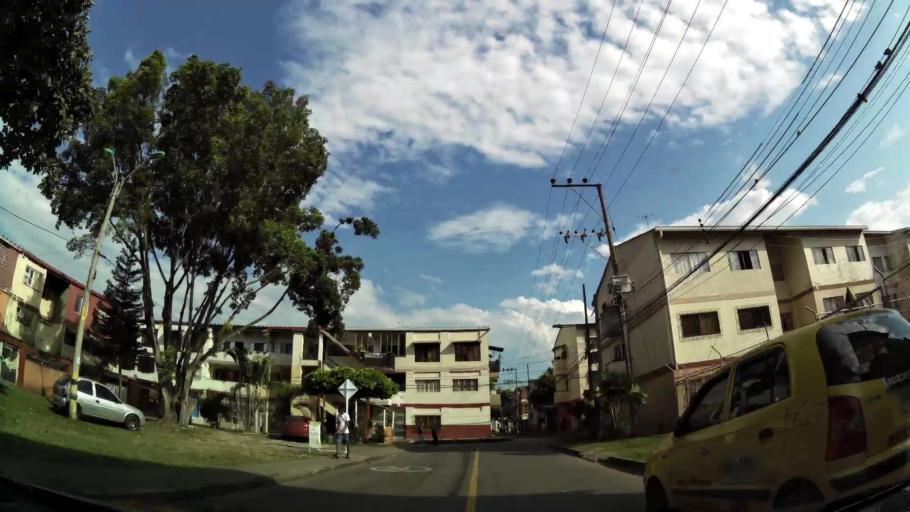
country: CO
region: Valle del Cauca
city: Cali
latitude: 3.4679
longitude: -76.5152
